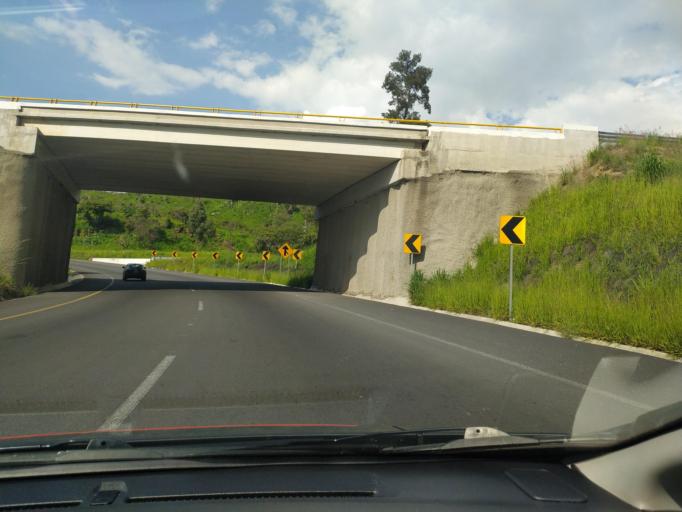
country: MX
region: Jalisco
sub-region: Acatlan de Juarez
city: Villa de los Ninos
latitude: 20.4236
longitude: -103.5533
